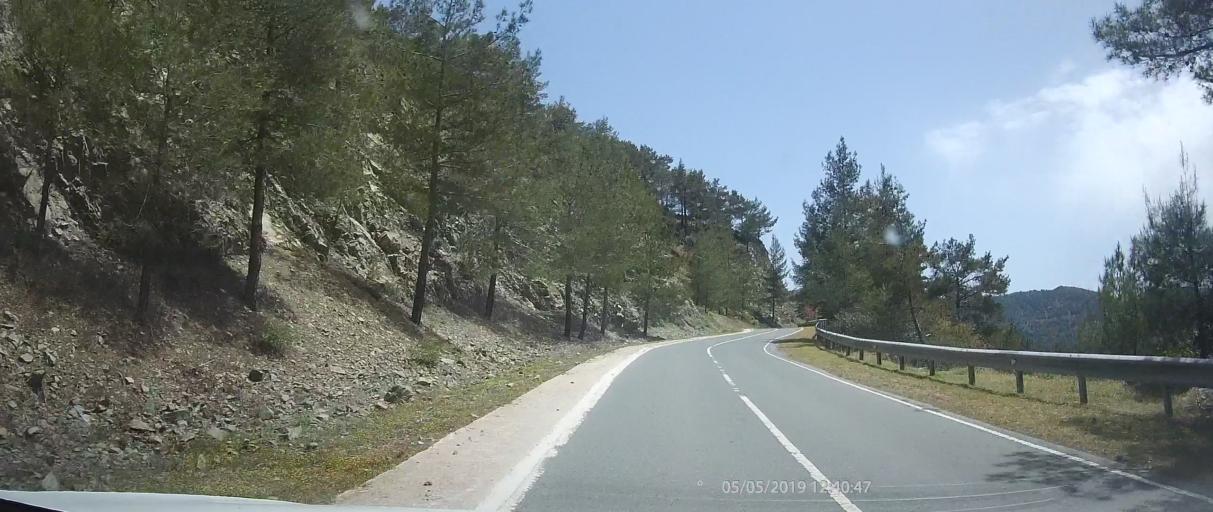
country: CY
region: Lefkosia
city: Kakopetria
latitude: 34.9877
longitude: 32.8030
